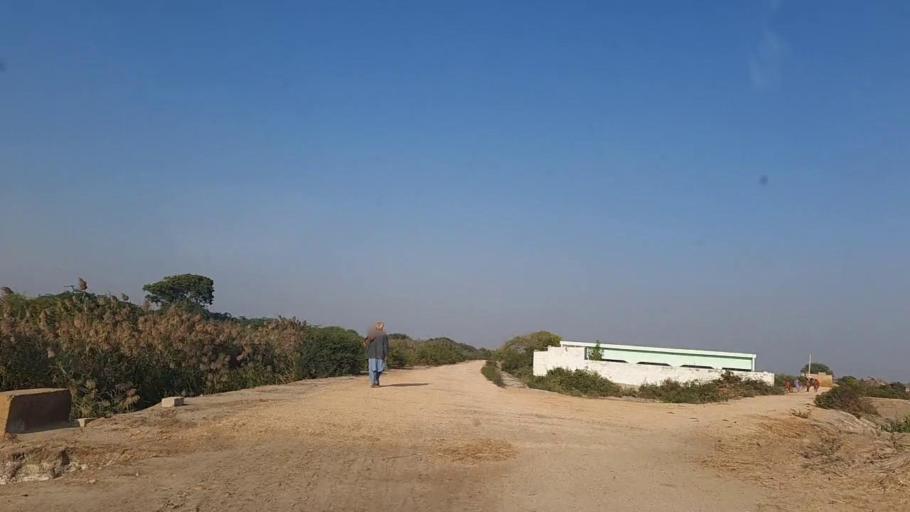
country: PK
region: Sindh
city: Thatta
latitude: 24.7260
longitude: 67.9494
